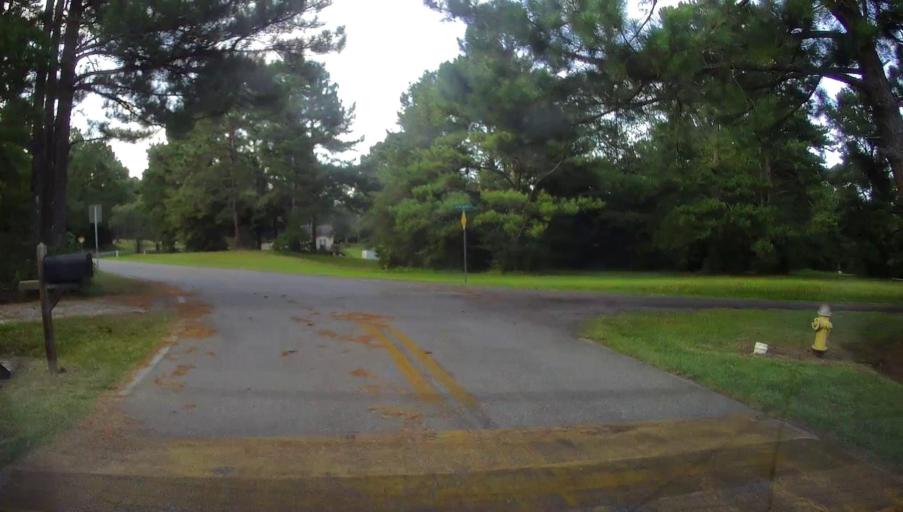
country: US
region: Georgia
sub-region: Monroe County
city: Forsyth
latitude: 33.0163
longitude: -83.9659
